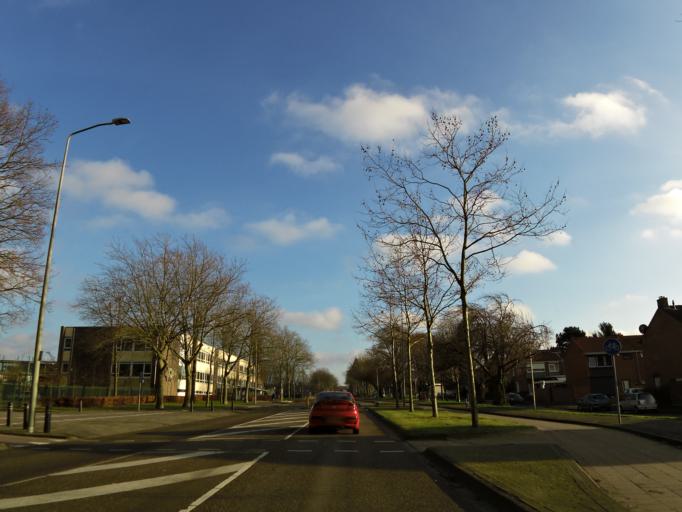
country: NL
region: Limburg
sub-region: Gemeente Heerlen
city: Heerlen
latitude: 50.8995
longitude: 5.9754
